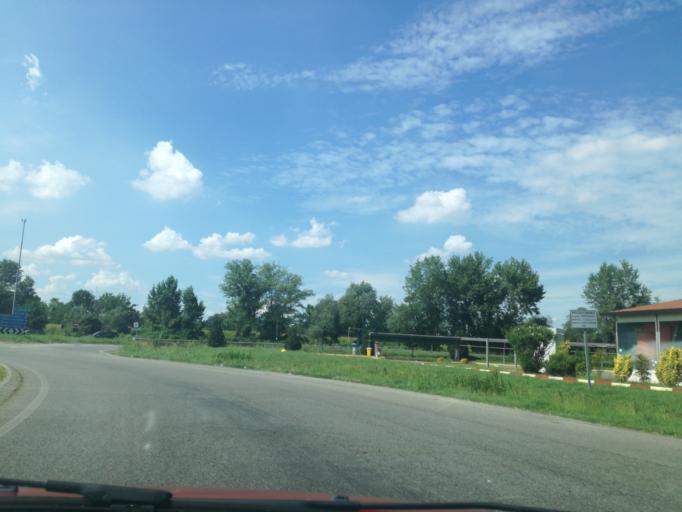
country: IT
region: Lombardy
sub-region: Citta metropolitana di Milano
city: Bellinzago Lombardo
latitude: 45.5477
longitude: 9.4525
